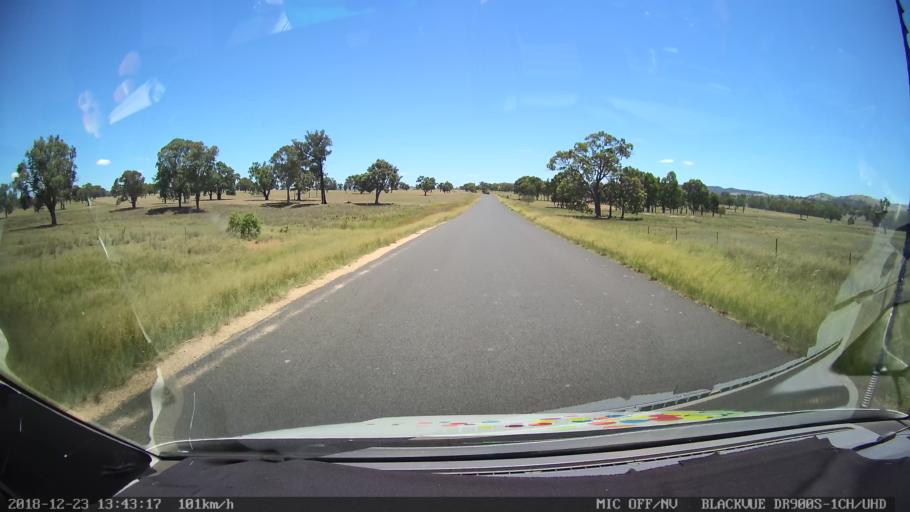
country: AU
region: New South Wales
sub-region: Tamworth Municipality
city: Manilla
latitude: -30.4851
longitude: 151.1523
